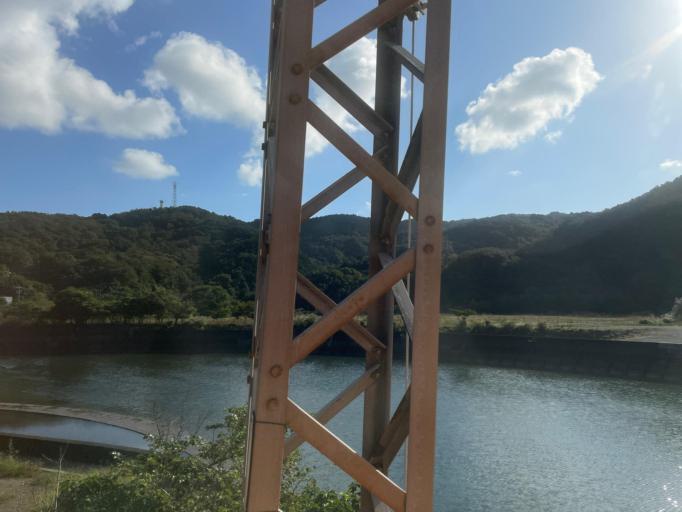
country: JP
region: Mie
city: Toba
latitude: 34.4556
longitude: 136.8433
